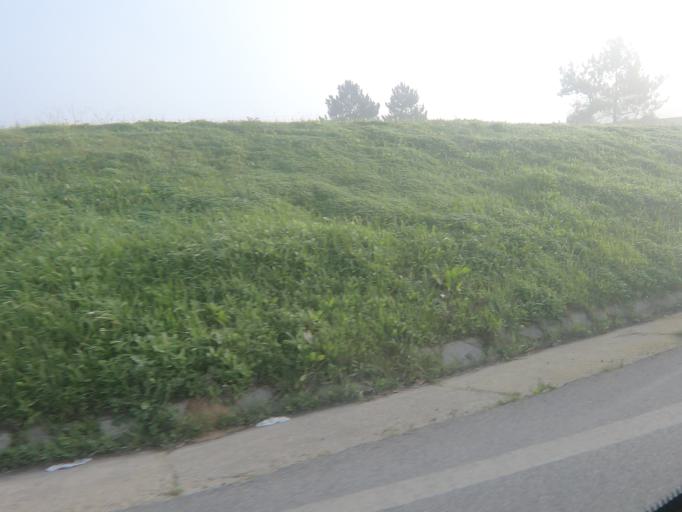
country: PT
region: Setubal
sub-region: Montijo
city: Montijo
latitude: 38.6838
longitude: -8.9418
